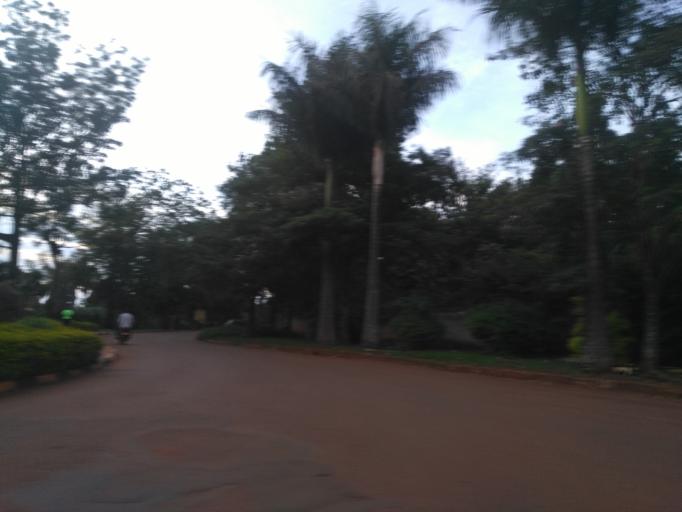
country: UG
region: Eastern Region
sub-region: Jinja District
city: Jinja
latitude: 0.4313
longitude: 33.1983
